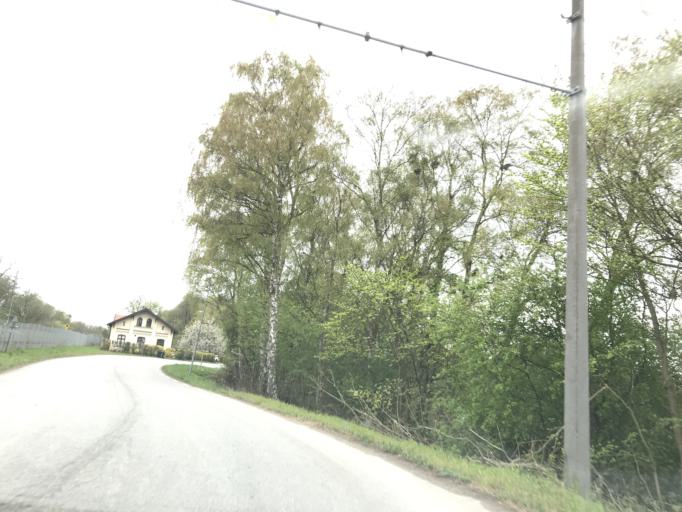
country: SE
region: Skane
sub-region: Trelleborgs Kommun
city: Anderslov
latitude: 55.4989
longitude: 13.3346
